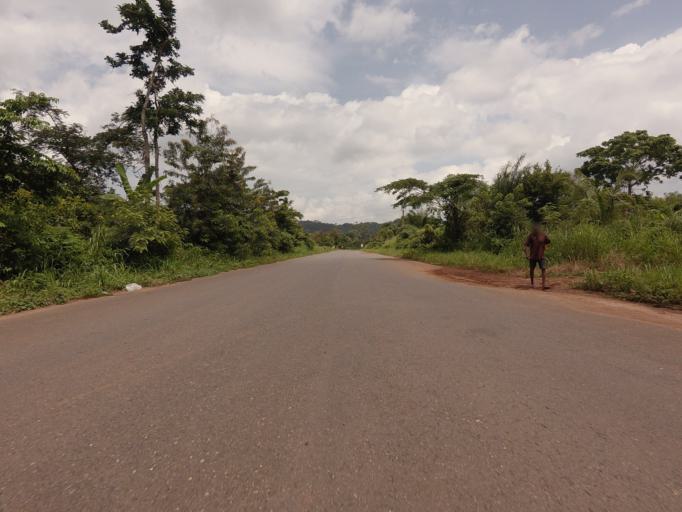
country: GH
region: Volta
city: Ho
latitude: 6.5180
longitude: 0.2193
